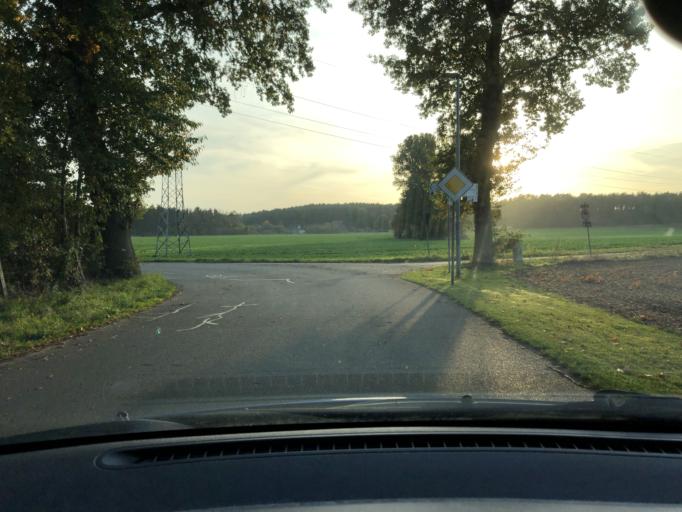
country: DE
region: Lower Saxony
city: Gohrde
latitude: 53.1388
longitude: 10.9536
